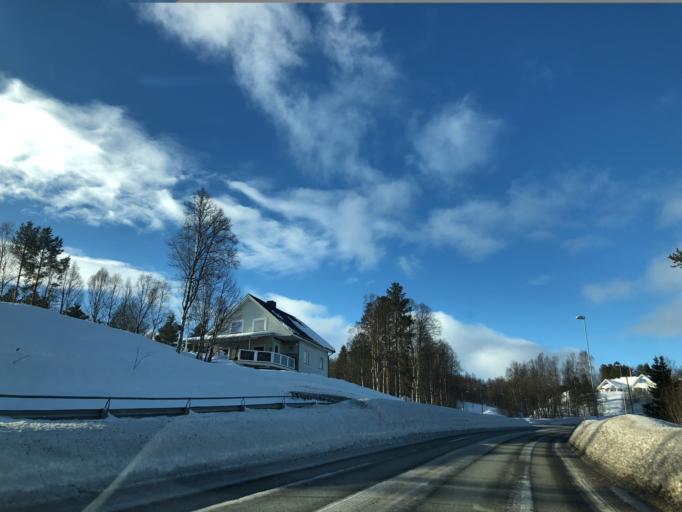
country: NO
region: Troms
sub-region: Malselv
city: Moen
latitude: 69.0495
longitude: 18.4919
